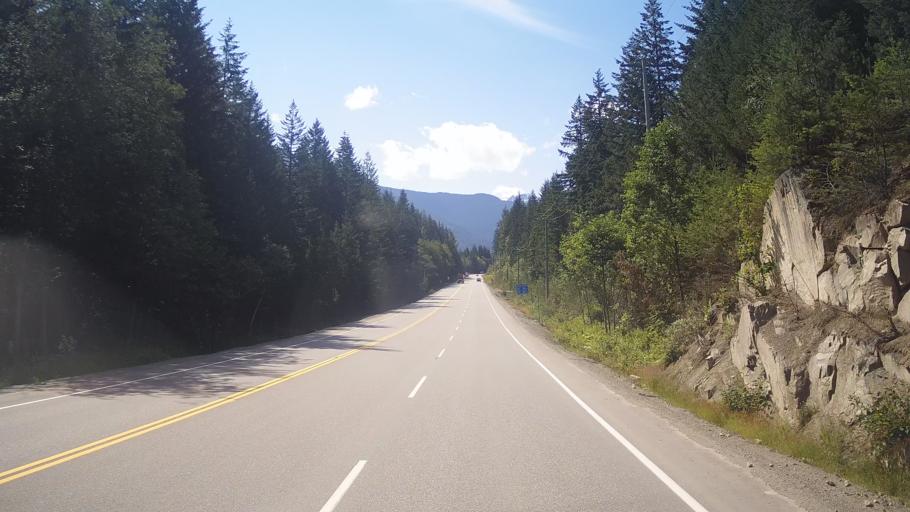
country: CA
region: British Columbia
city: Whistler
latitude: 50.2065
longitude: -122.8823
